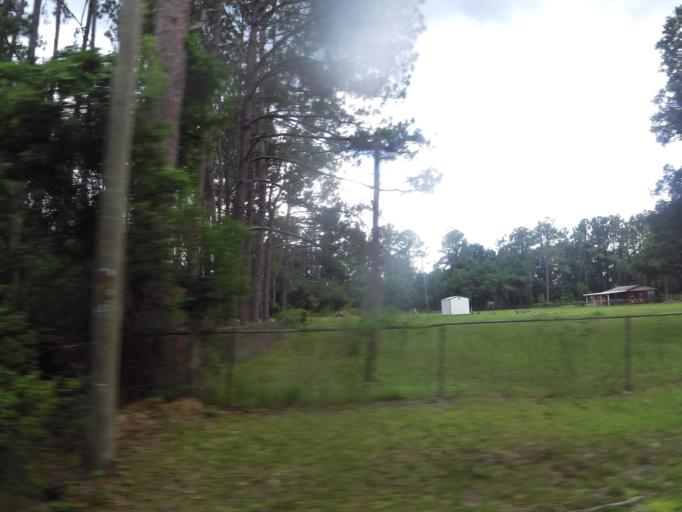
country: US
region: Florida
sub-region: Duval County
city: Baldwin
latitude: 30.3388
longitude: -81.8753
